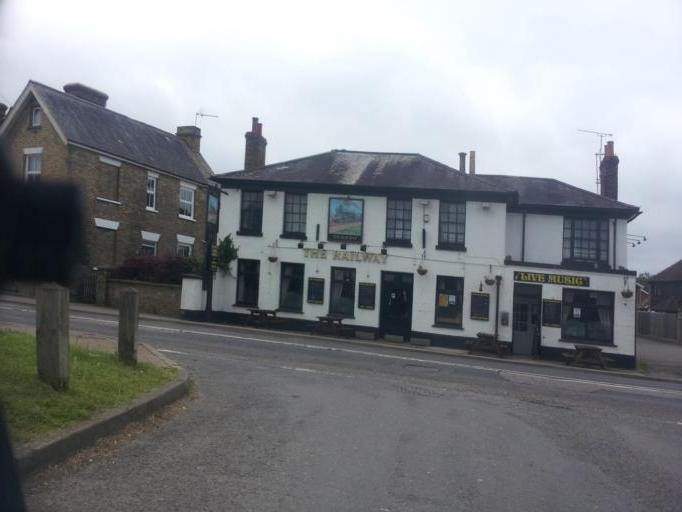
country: GB
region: England
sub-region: Kent
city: Wateringbury
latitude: 51.2496
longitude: 0.4210
